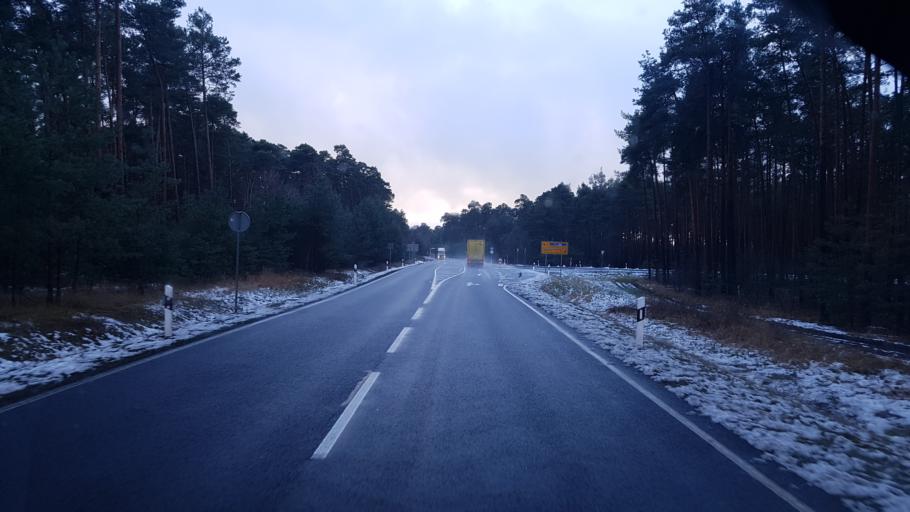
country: DE
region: Brandenburg
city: Janschwalde
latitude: 51.8482
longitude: 14.5136
